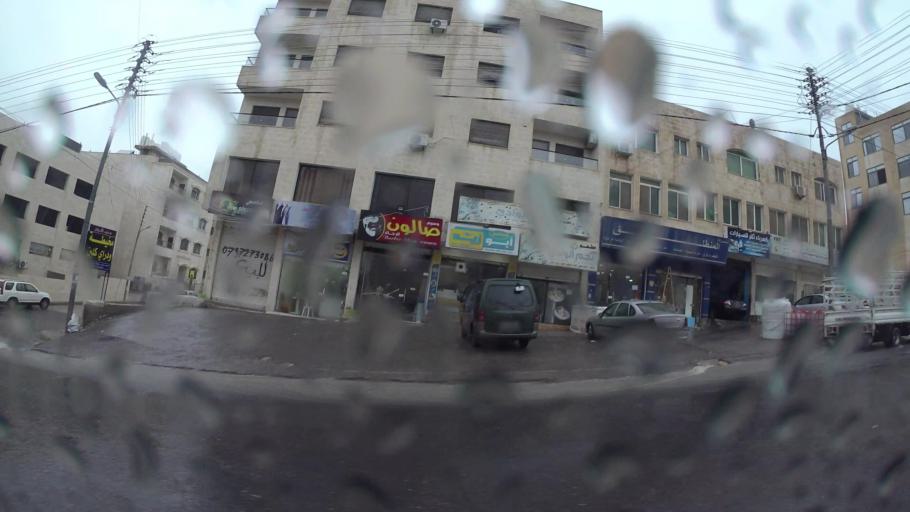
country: JO
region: Amman
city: Al Jubayhah
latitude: 32.0498
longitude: 35.8818
